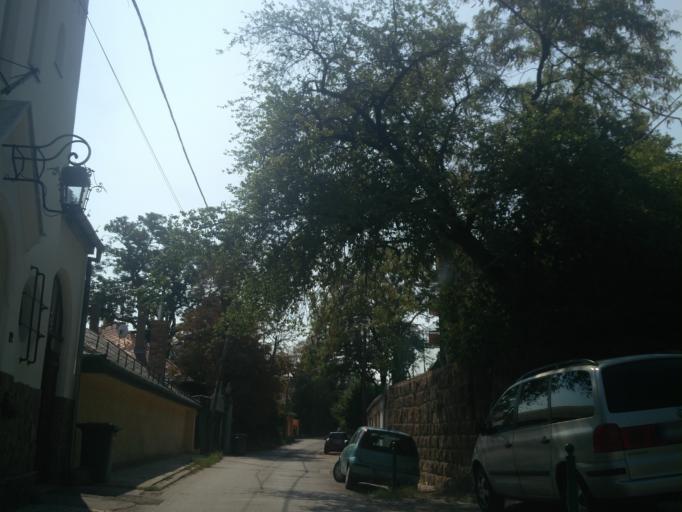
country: HU
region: Budapest
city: Budapest XII. keruelet
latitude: 47.5019
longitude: 18.9999
